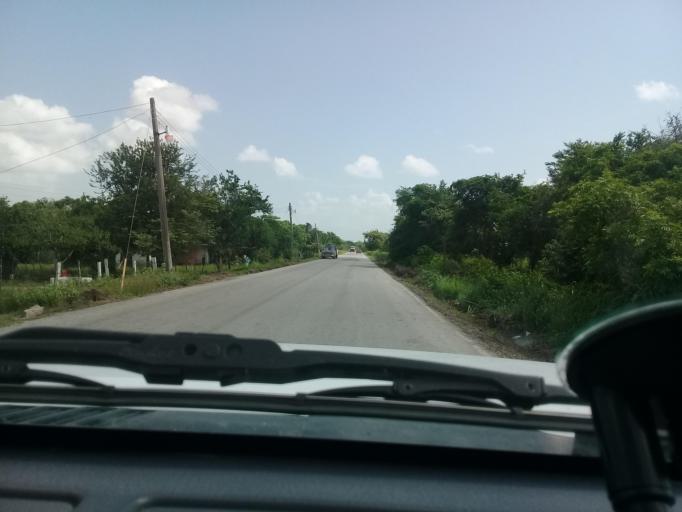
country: MX
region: Veracruz
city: Moralillo
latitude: 22.1826
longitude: -97.9468
